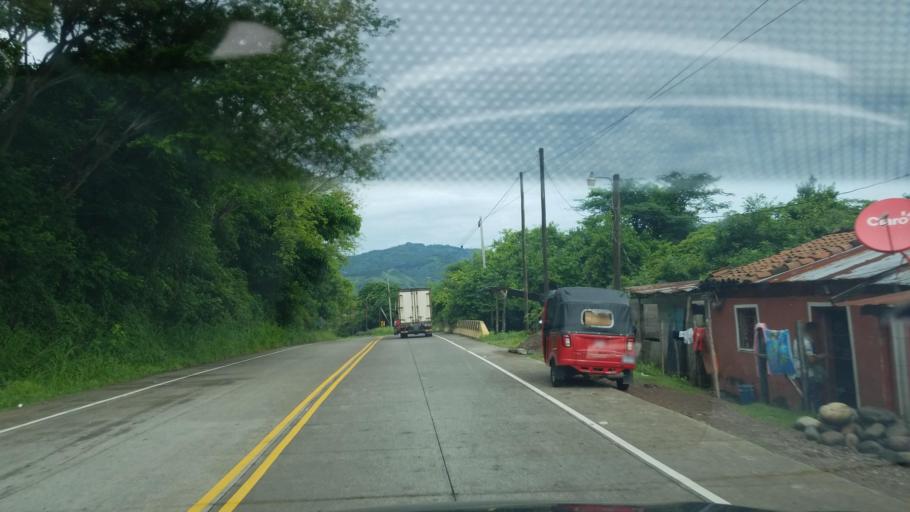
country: HN
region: Choluteca
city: Pespire
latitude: 13.6501
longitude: -87.3665
